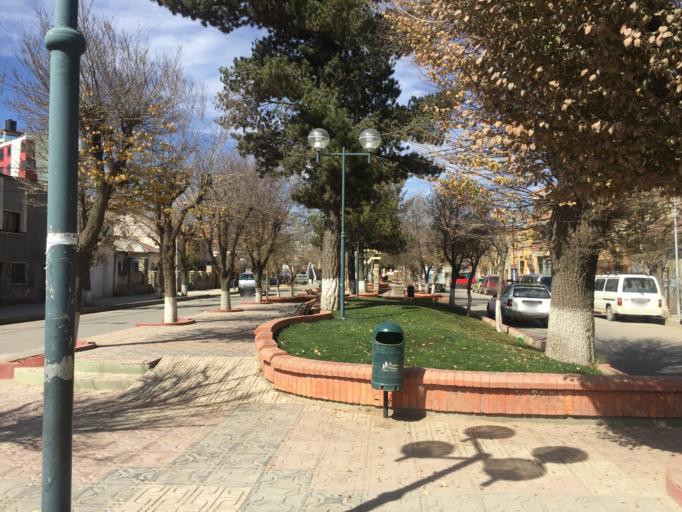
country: BO
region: Oruro
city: Oruro
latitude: -17.9534
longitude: -67.1097
